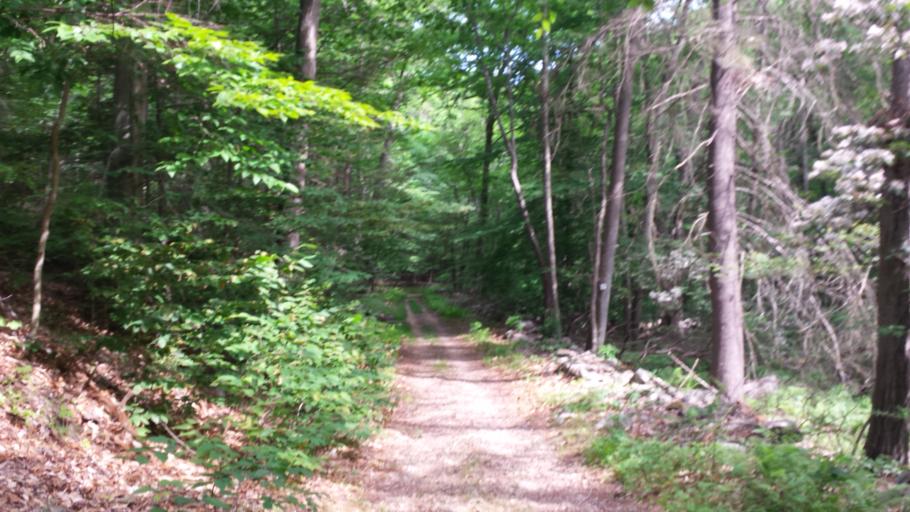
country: US
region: New York
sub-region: Westchester County
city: Pound Ridge
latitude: 41.2378
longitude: -73.5876
